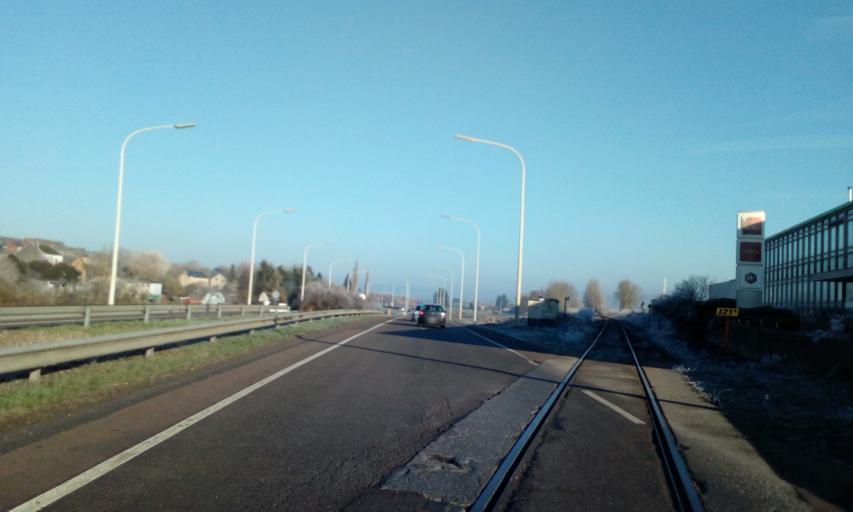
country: BE
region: Wallonia
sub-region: Province de Namur
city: Couvin
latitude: 50.0742
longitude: 4.5108
